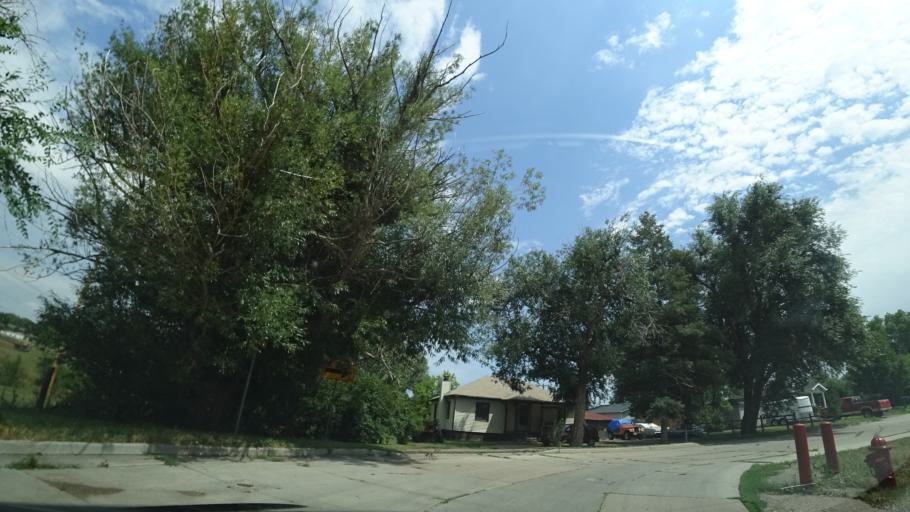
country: US
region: Colorado
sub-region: Jefferson County
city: Lakewood
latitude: 39.7003
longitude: -105.0682
